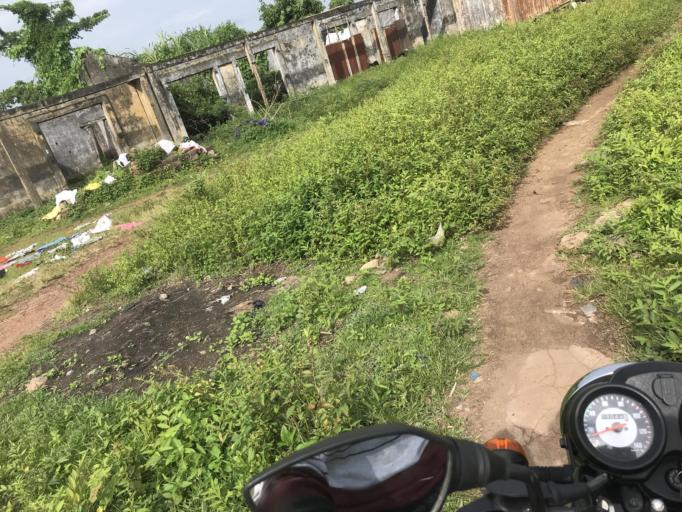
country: SL
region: Eastern Province
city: Buedu
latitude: 8.4633
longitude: -10.3381
